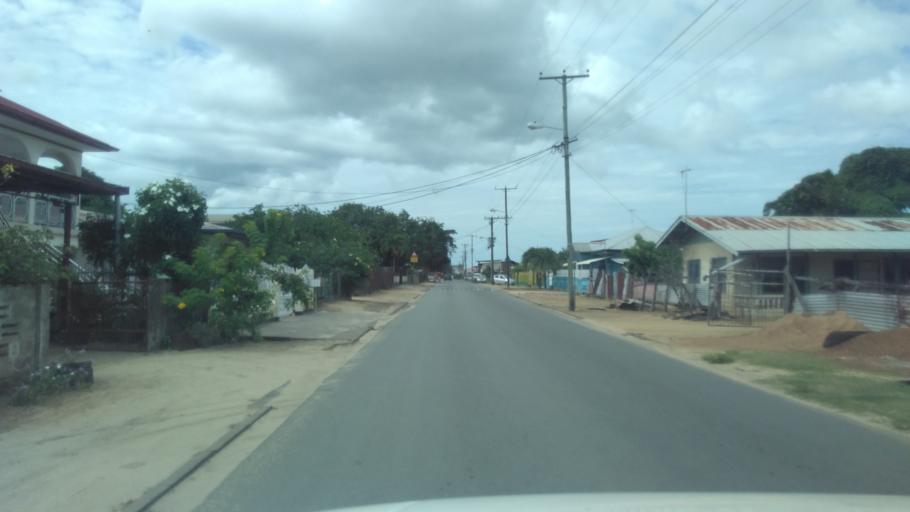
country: SR
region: Paramaribo
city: Paramaribo
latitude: 5.8493
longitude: -55.1279
